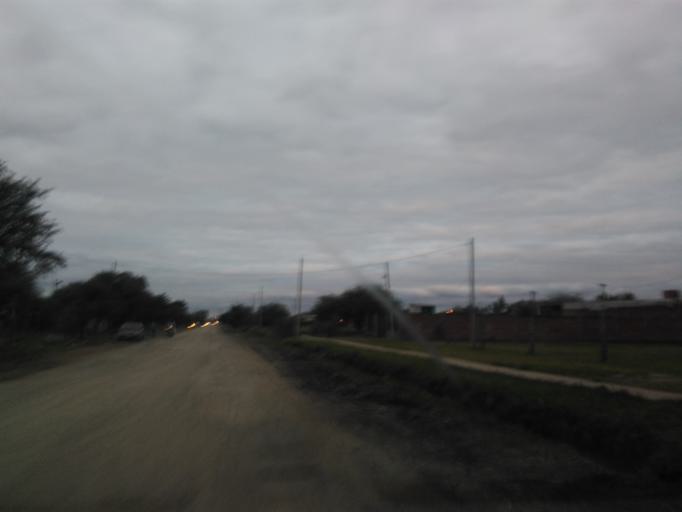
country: AR
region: Chaco
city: Resistencia
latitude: -27.4791
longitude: -59.0090
